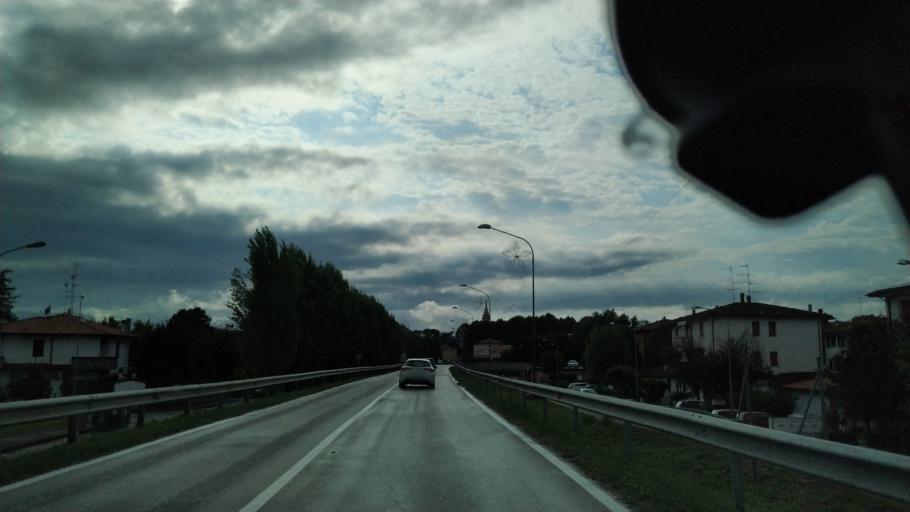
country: IT
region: Emilia-Romagna
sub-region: Provincia di Ferrara
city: Sant'Agostino
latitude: 44.7928
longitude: 11.3926
